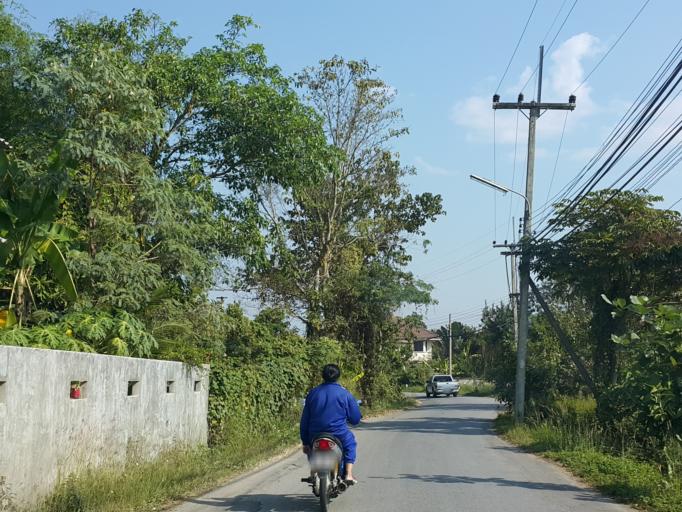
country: TH
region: Chiang Mai
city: San Sai
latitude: 18.8482
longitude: 99.0990
